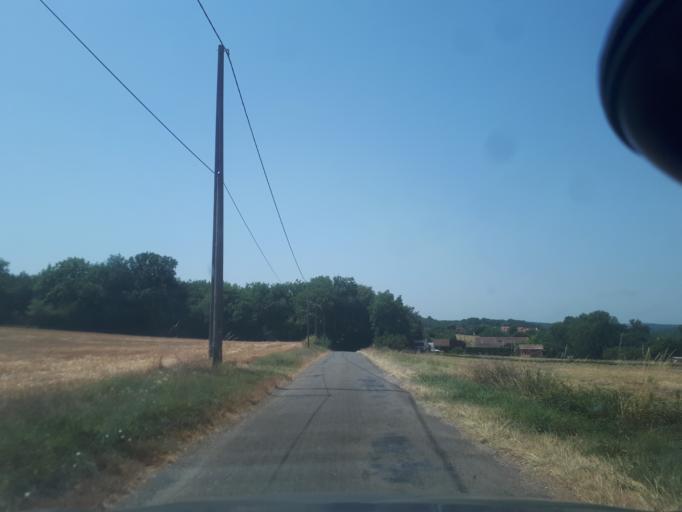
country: FR
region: Midi-Pyrenees
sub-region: Departement du Lot
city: Salviac
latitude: 44.7343
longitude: 1.2944
